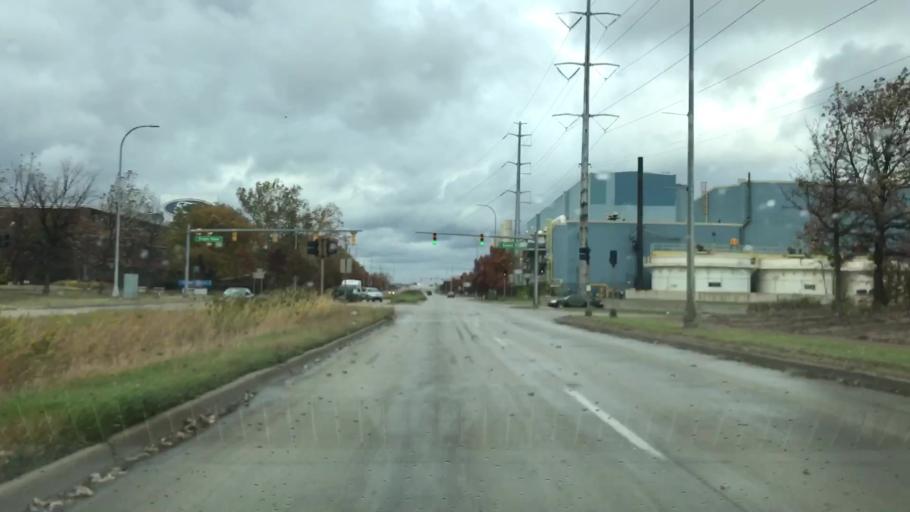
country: US
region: Michigan
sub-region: Wayne County
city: Dearborn
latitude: 42.3092
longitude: -83.1567
